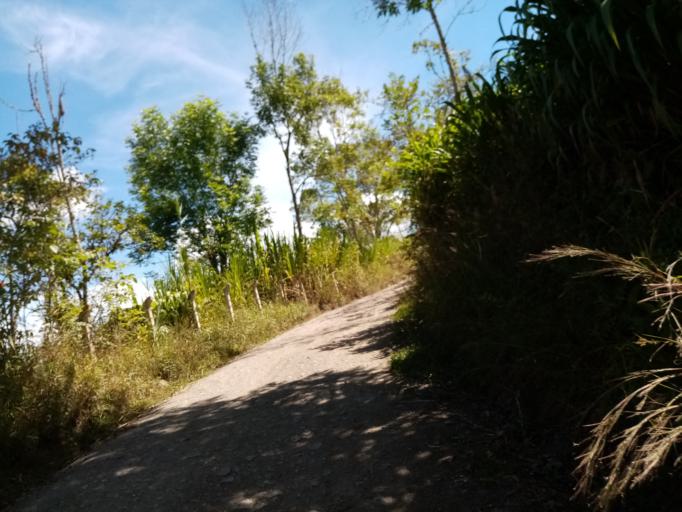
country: CO
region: Cundinamarca
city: Tenza
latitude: 5.0735
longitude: -73.4278
